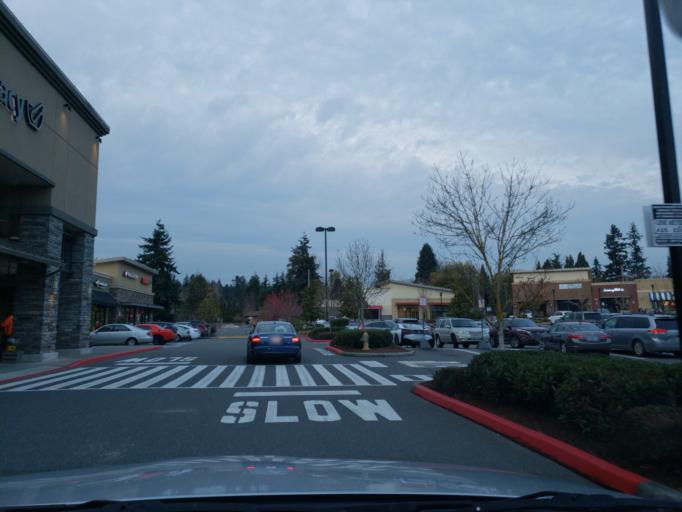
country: US
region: Washington
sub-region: King County
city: Bothell
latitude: 47.7790
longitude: -122.2203
